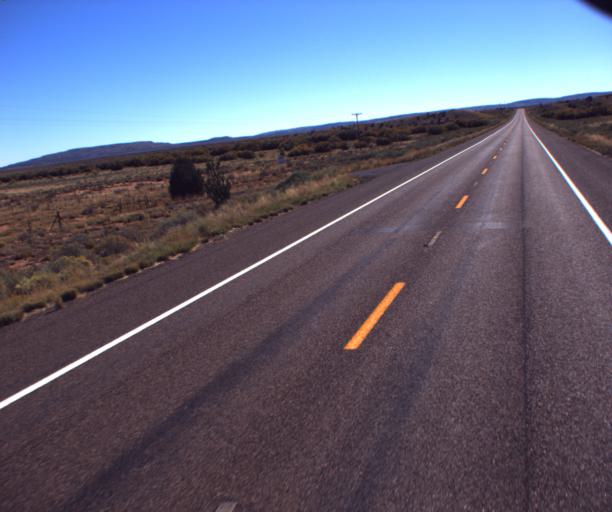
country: US
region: Arizona
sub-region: Apache County
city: Saint Johns
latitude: 34.6321
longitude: -109.6803
